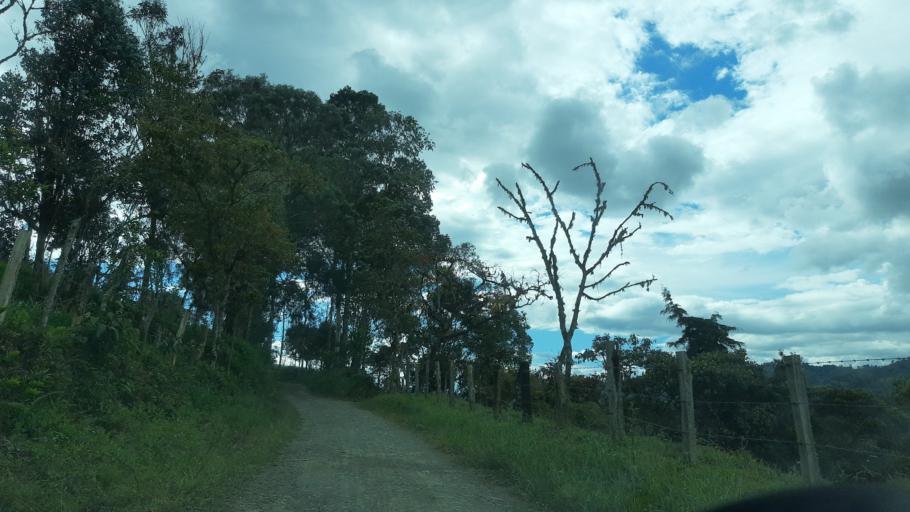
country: CO
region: Boyaca
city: Garagoa
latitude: 5.0349
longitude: -73.3312
